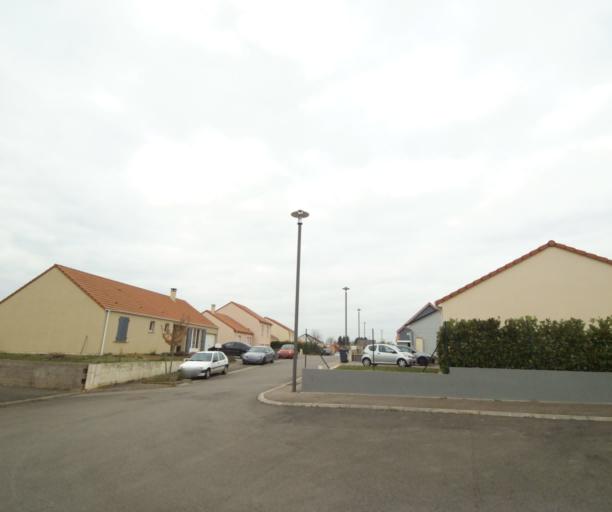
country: FR
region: Lorraine
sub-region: Departement de Meurthe-et-Moselle
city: Mancieulles
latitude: 49.2740
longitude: 5.9067
